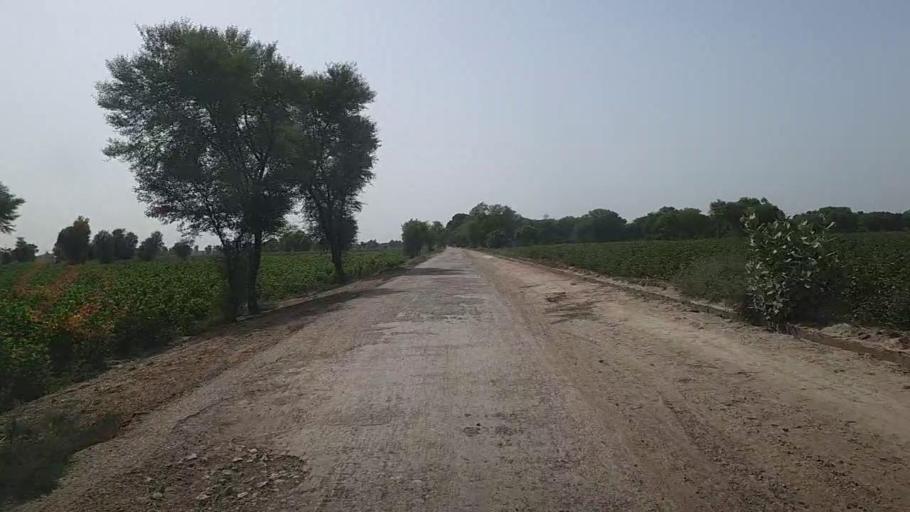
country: PK
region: Sindh
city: Pad Idan
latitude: 26.7685
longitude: 68.3171
